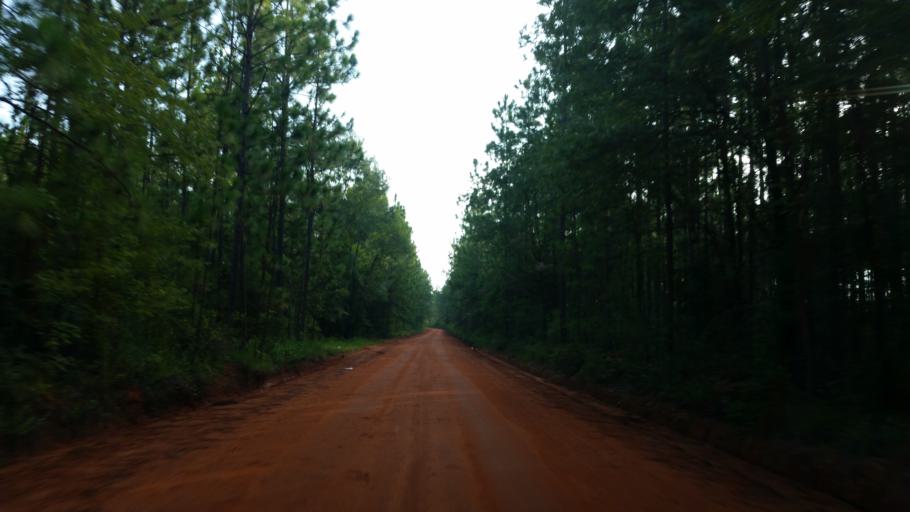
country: US
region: Alabama
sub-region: Escambia County
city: Atmore
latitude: 30.9279
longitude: -87.5721
